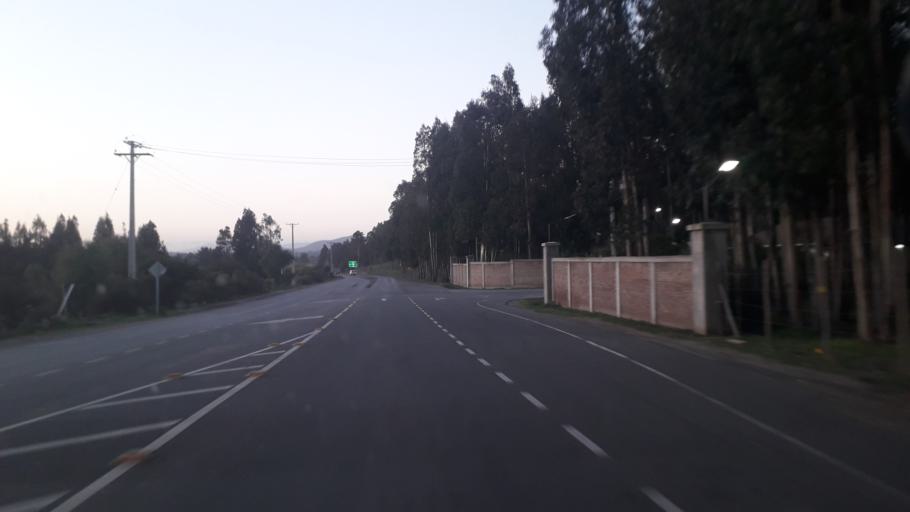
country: CL
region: Valparaiso
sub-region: Provincia de Quillota
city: Hacienda La Calera
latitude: -32.7469
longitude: -71.4183
